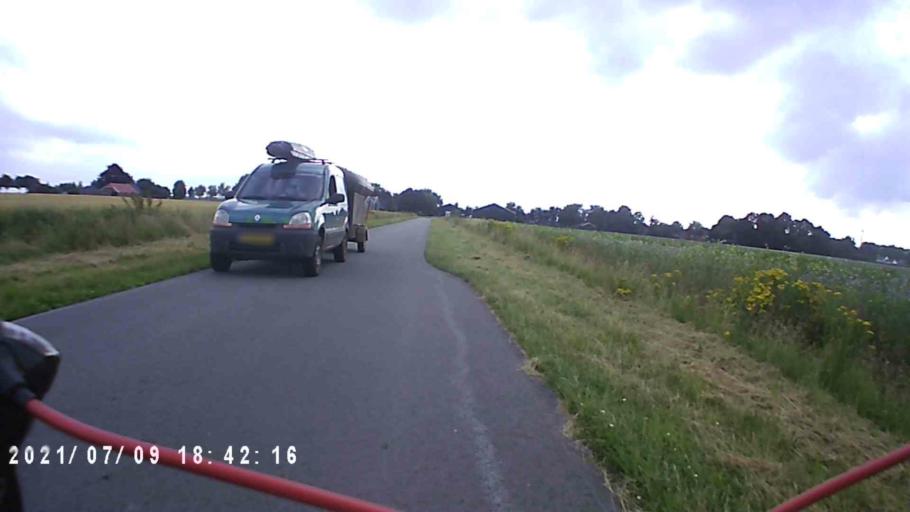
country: NL
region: Groningen
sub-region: Gemeente Veendam
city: Veendam
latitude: 53.0800
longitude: 6.9255
